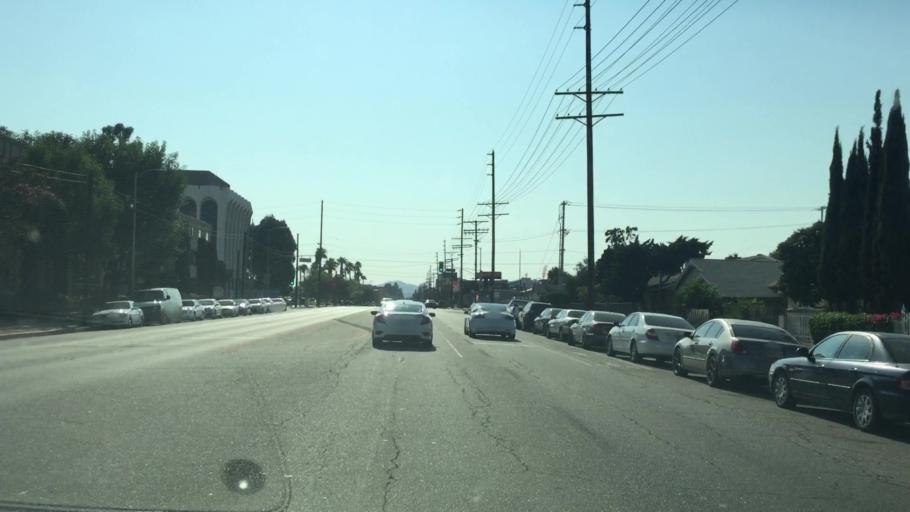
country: US
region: California
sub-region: Los Angeles County
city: Northridge
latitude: 34.2575
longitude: -118.4968
